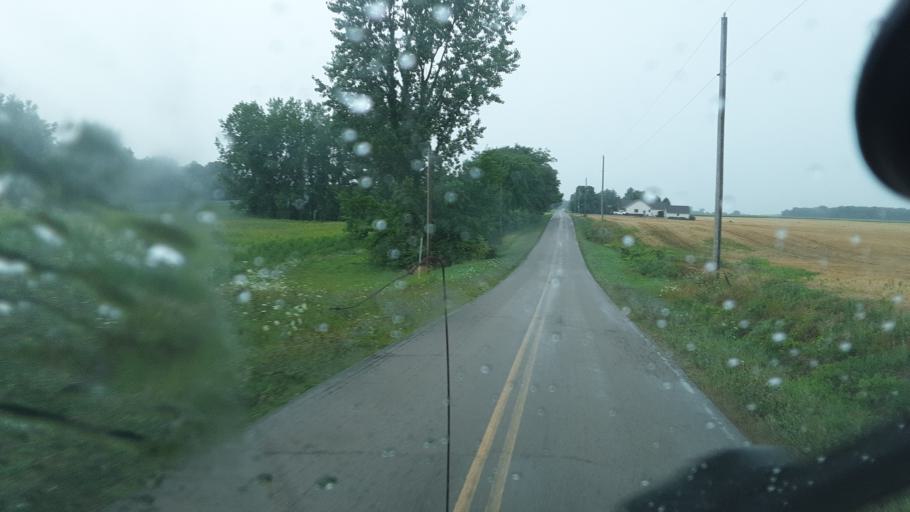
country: US
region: Ohio
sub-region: Williams County
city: Edgerton
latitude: 41.4261
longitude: -84.7891
